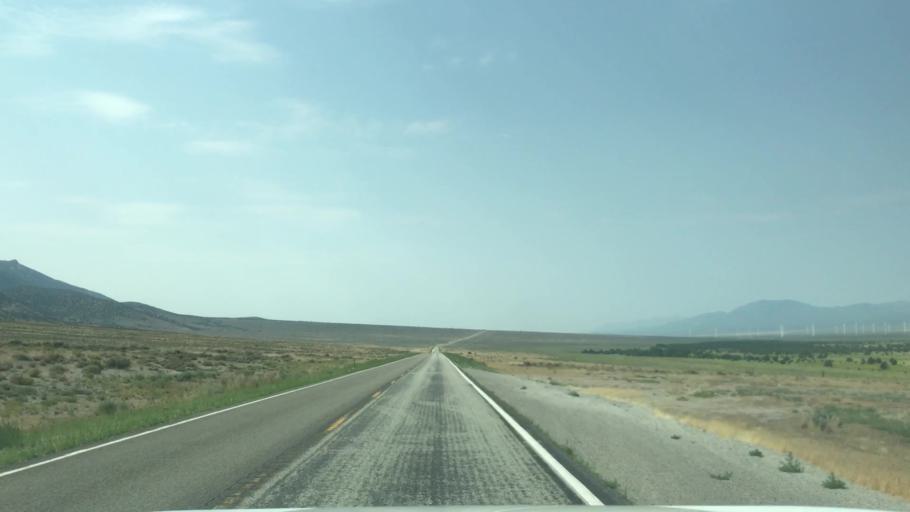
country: US
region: Nevada
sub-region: White Pine County
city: McGill
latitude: 39.1481
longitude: -114.4146
